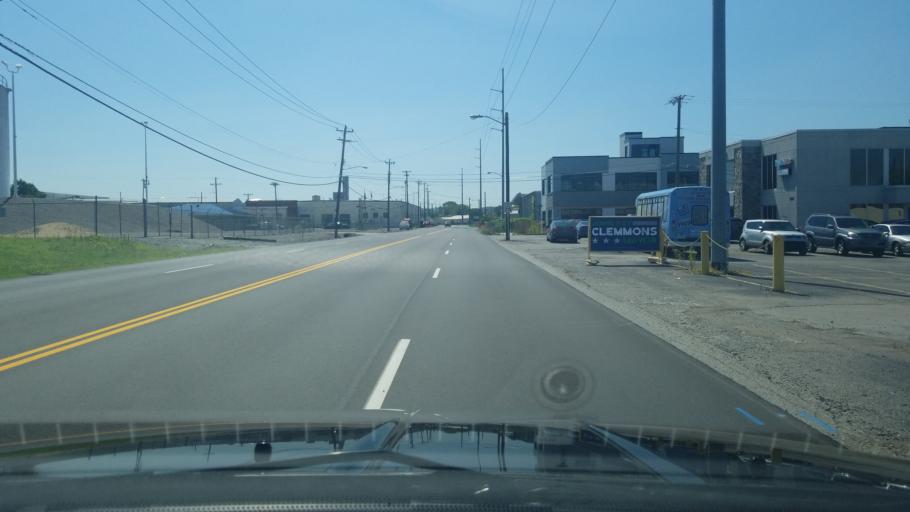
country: US
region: Tennessee
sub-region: Davidson County
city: Belle Meade
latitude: 36.1688
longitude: -86.8613
